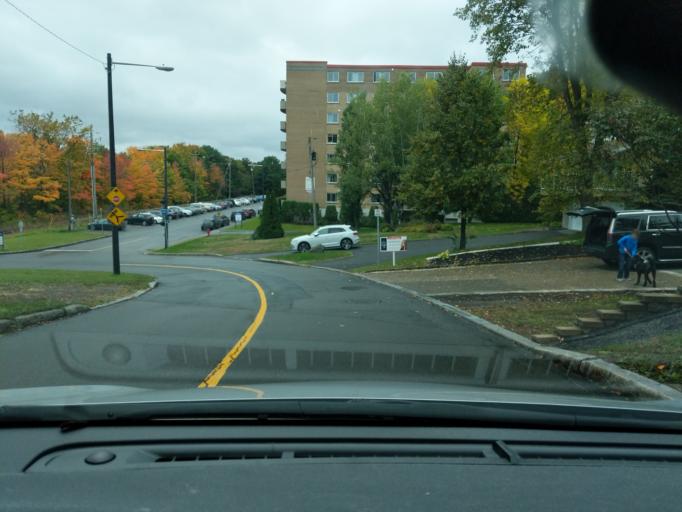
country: CA
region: Quebec
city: Quebec
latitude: 46.7632
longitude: -71.2666
